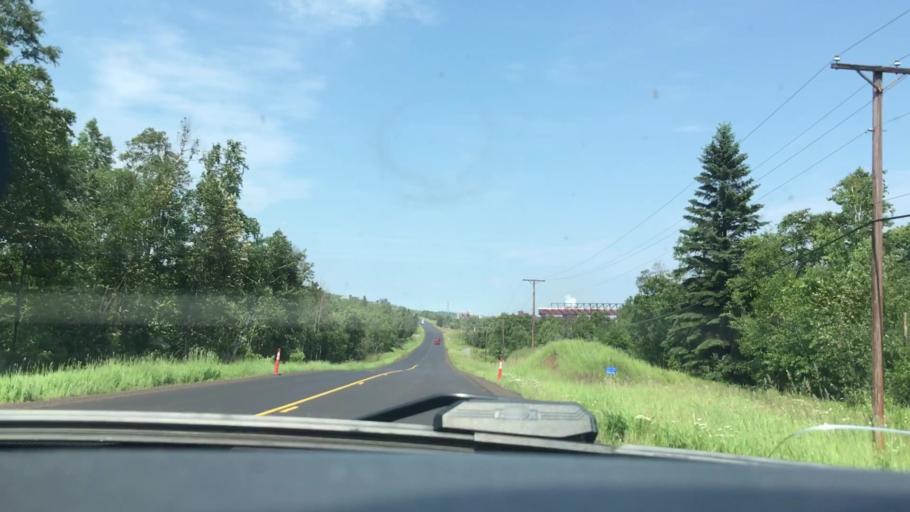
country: US
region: Minnesota
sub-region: Lake County
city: Silver Bay
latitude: 47.2751
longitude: -91.2753
